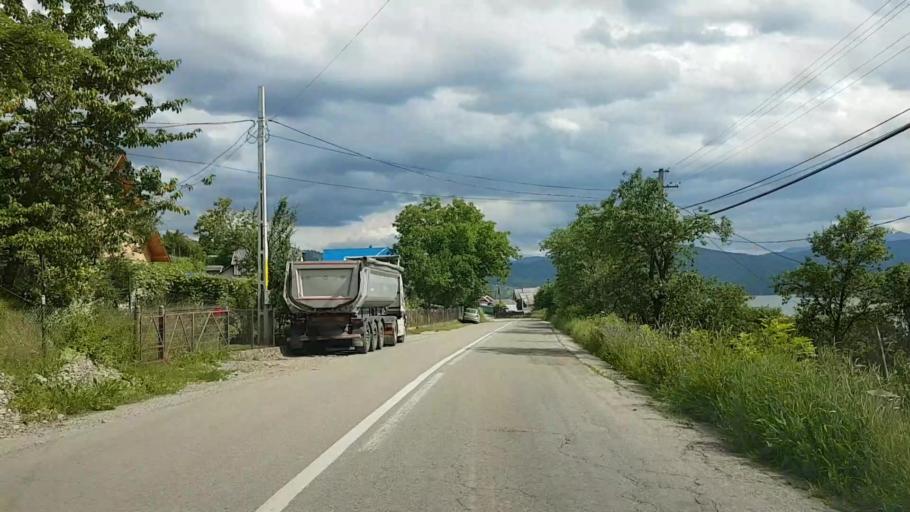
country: RO
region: Neamt
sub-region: Comuna Hangu
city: Hangu
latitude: 47.0252
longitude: 26.0688
